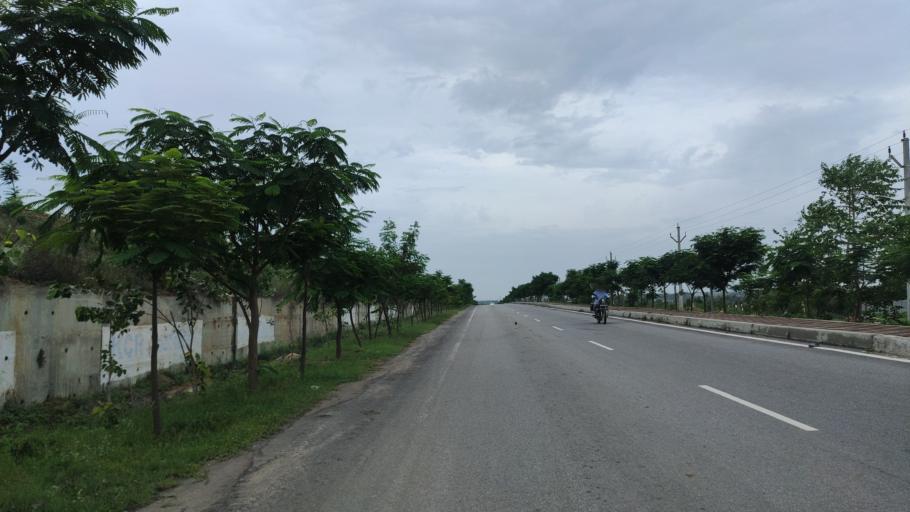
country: IN
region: Telangana
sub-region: Rangareddi
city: Secunderabad
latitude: 17.5794
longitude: 78.5886
